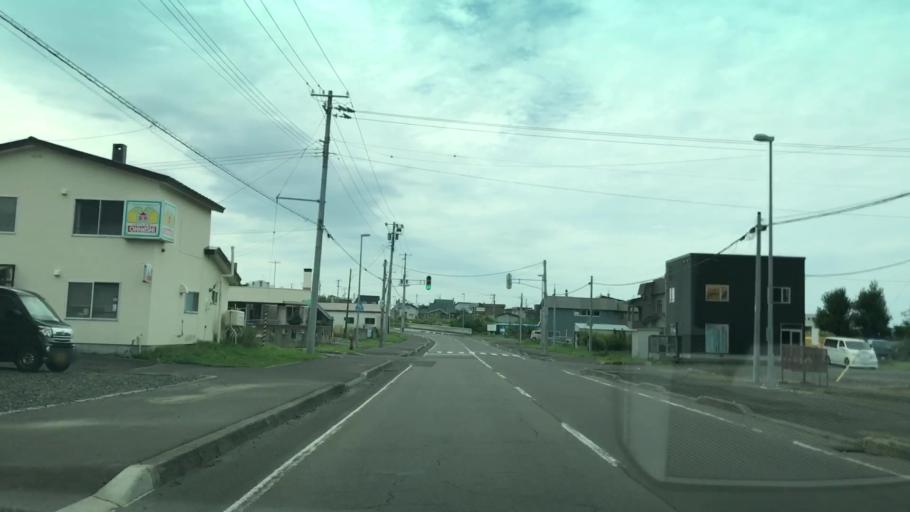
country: JP
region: Hokkaido
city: Iwanai
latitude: 42.9768
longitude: 140.5025
